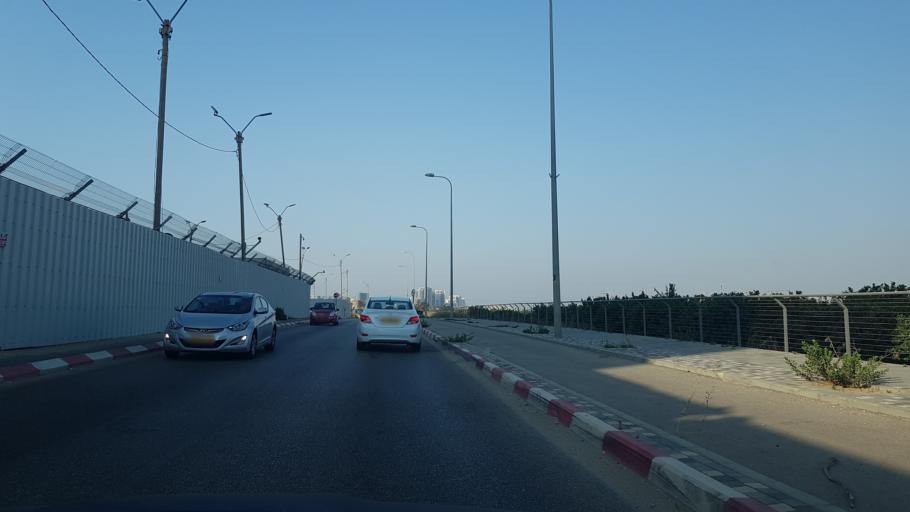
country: IL
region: Tel Aviv
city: Herzliyya
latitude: 32.1435
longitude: 34.8065
